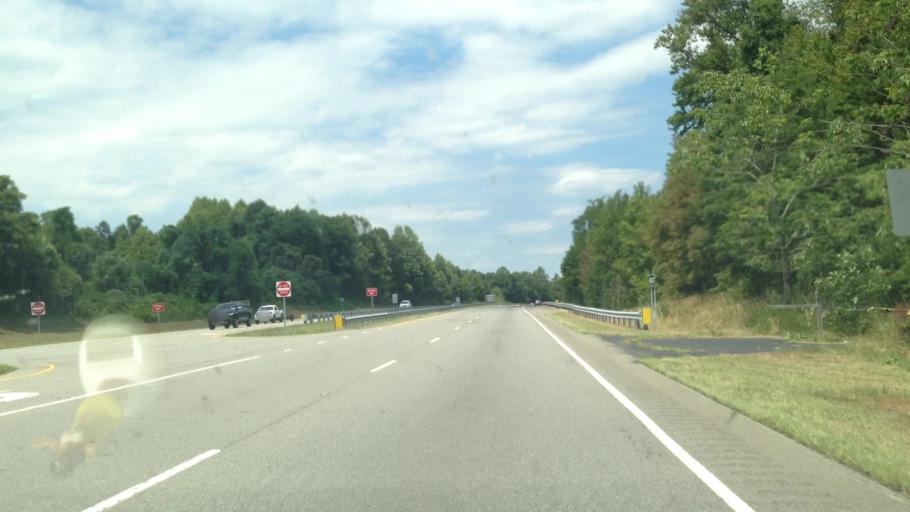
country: US
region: North Carolina
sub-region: Rockingham County
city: Stoneville
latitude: 36.5365
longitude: -79.9132
